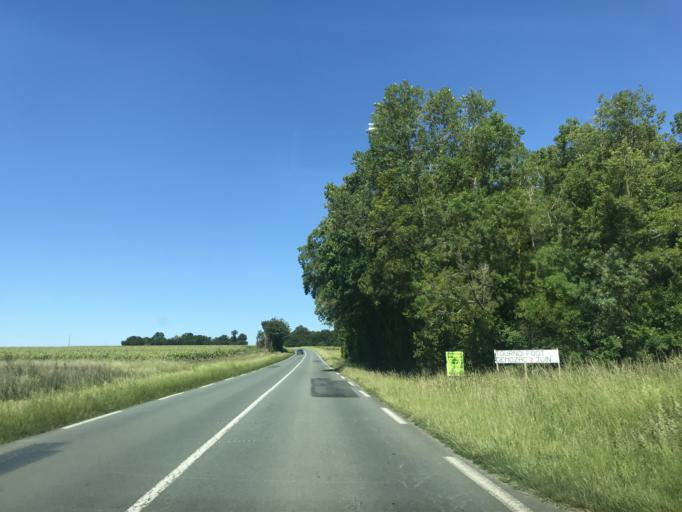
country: FR
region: Poitou-Charentes
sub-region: Departement de la Charente-Maritime
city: Gemozac
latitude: 45.5714
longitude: -0.6262
